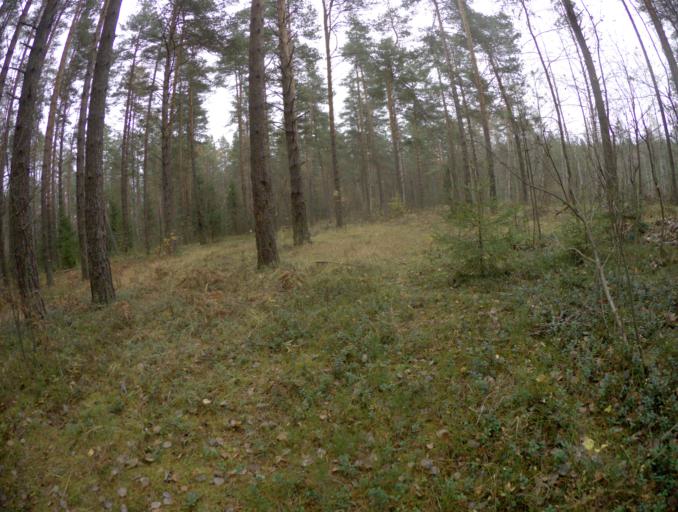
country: RU
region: Vladimir
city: Krasnyy Oktyabr'
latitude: 56.0092
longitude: 38.8360
